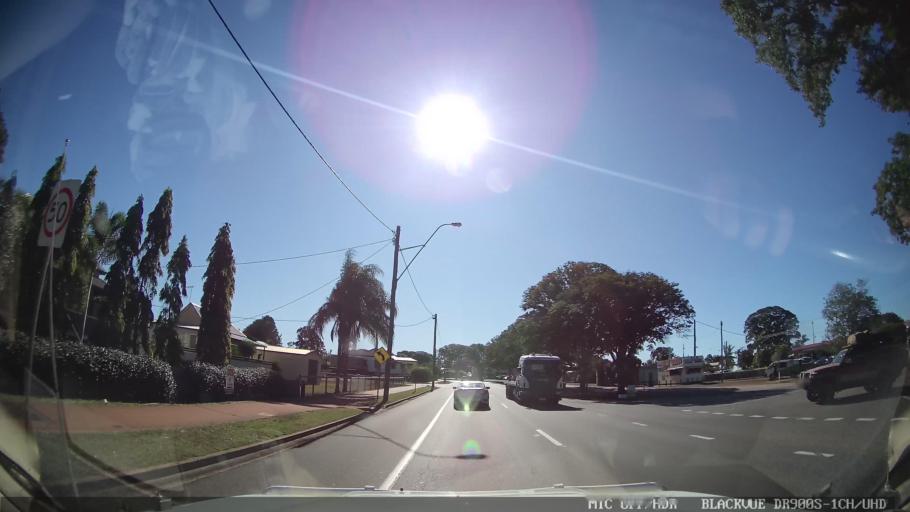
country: AU
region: Queensland
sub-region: Bundaberg
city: Childers
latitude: -25.2345
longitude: 152.2739
